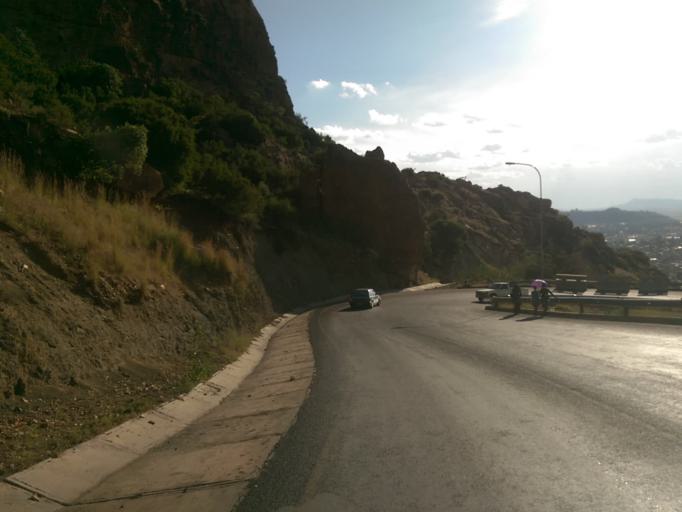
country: LS
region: Maseru
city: Maseru
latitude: -29.3147
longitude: 27.5468
